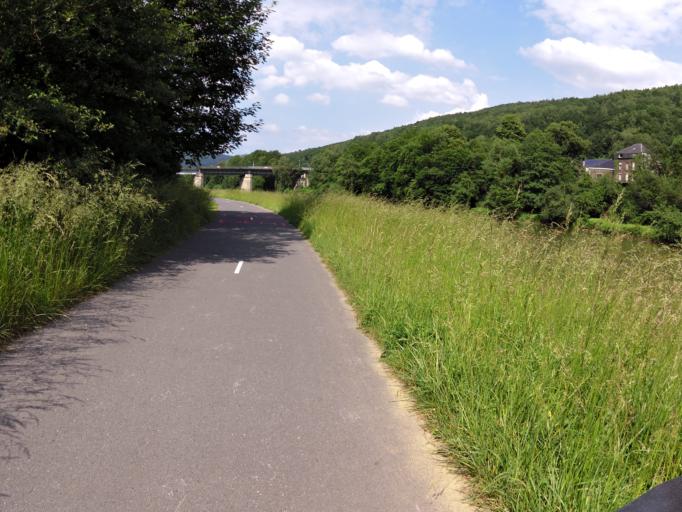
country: FR
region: Champagne-Ardenne
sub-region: Departement des Ardennes
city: Montherme
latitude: 49.8636
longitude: 4.7364
